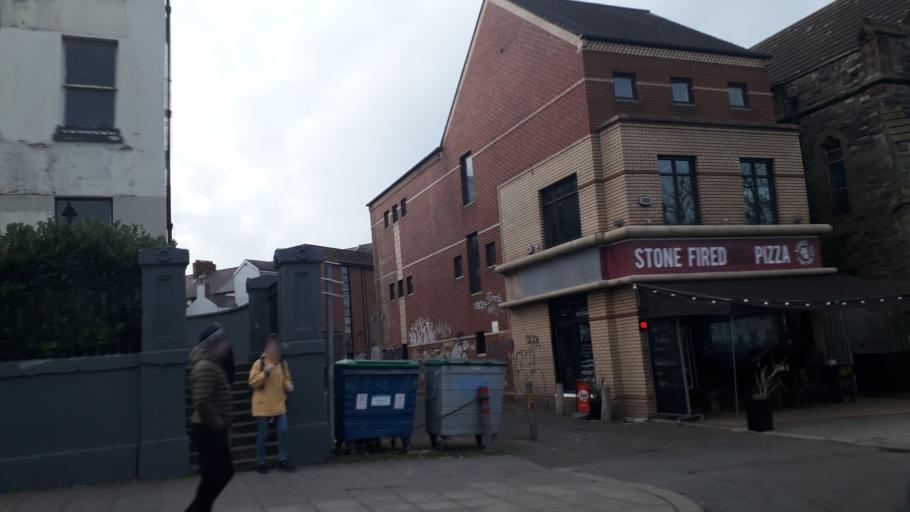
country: GB
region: Northern Ireland
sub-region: City of Belfast
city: Belfast
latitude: 54.5876
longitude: -5.9357
